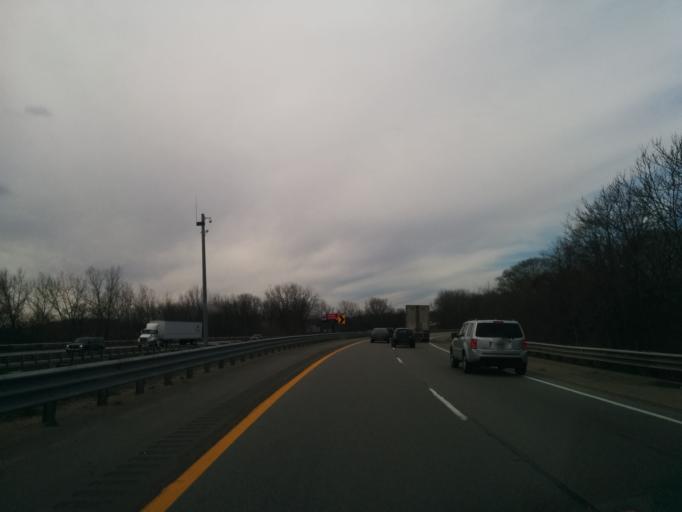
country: US
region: Michigan
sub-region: Kent County
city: Wyoming
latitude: 42.9344
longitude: -85.7234
